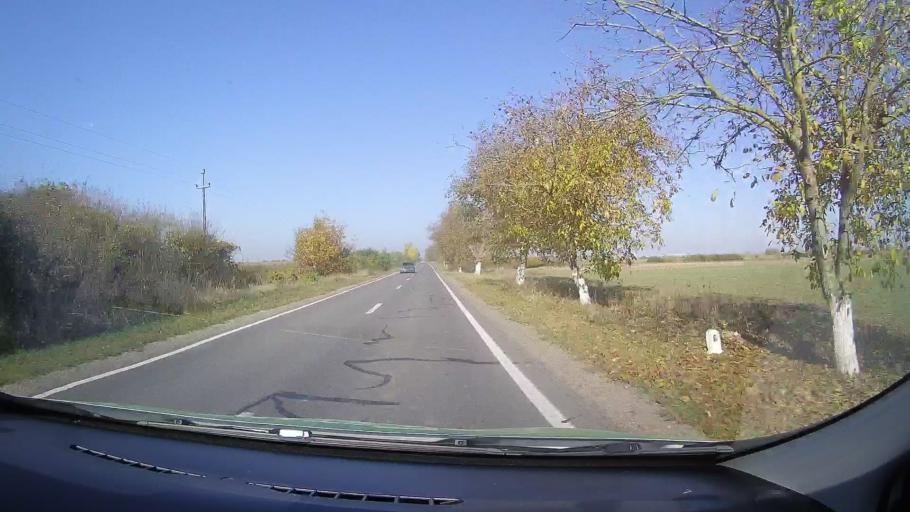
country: RO
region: Satu Mare
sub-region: Comuna Urziceni
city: Urziceni
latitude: 47.7137
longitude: 22.4240
